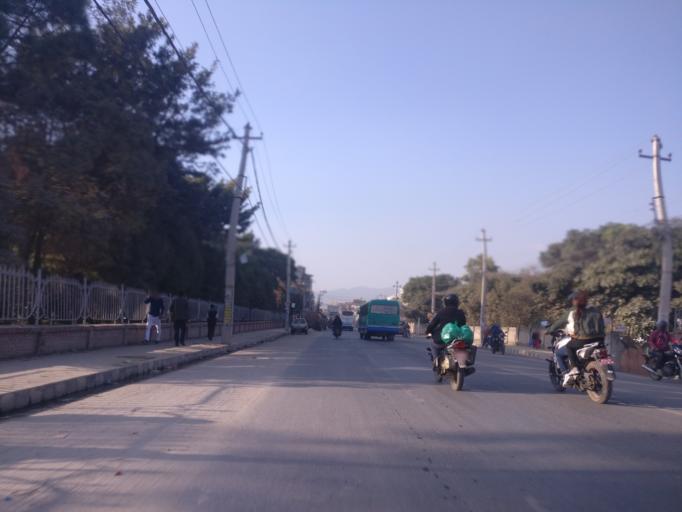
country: NP
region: Central Region
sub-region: Bagmati Zone
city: Patan
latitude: 27.6562
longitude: 85.3269
